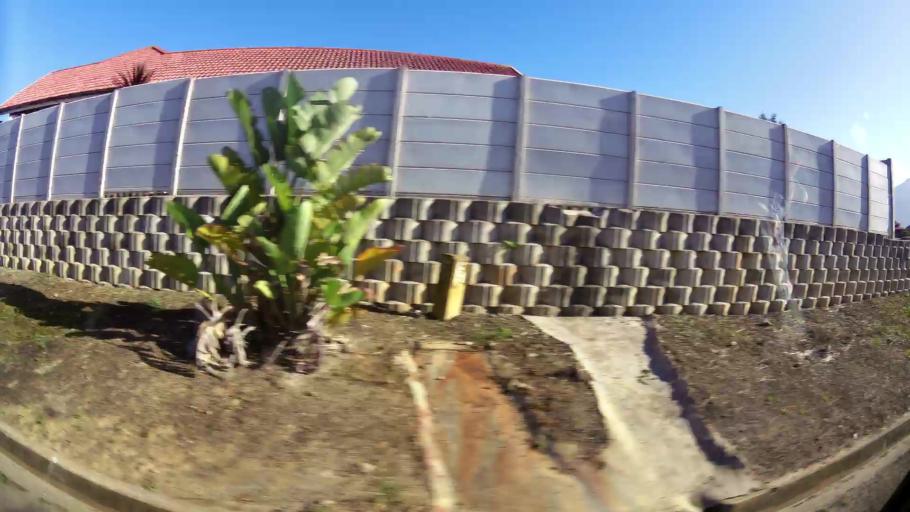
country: ZA
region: Western Cape
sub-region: Eden District Municipality
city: George
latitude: -33.9714
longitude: 22.4403
